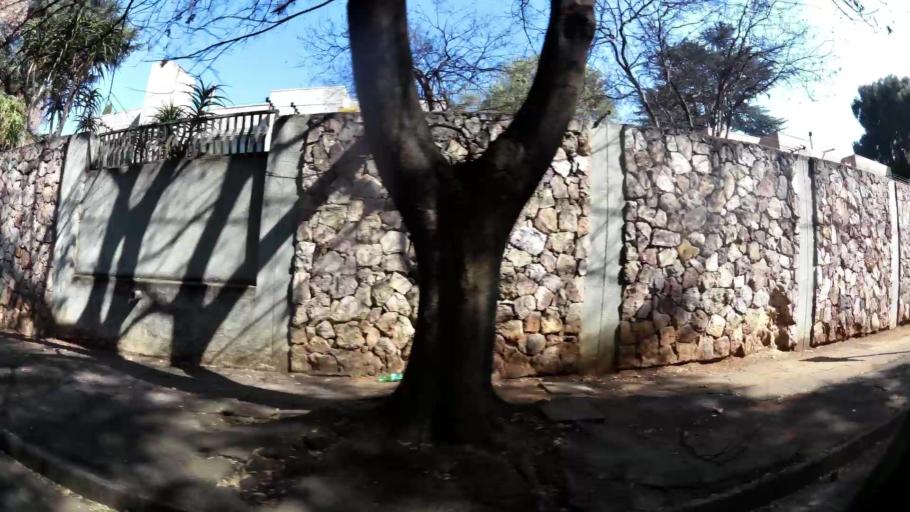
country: ZA
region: Gauteng
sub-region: City of Johannesburg Metropolitan Municipality
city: Johannesburg
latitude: -26.1590
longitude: 28.0277
